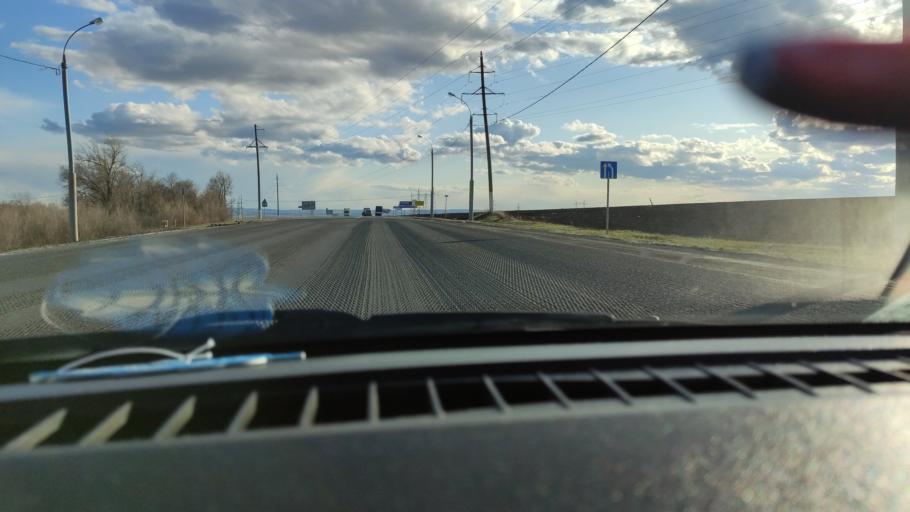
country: RU
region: Saratov
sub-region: Saratovskiy Rayon
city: Saratov
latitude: 51.7681
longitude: 46.0800
